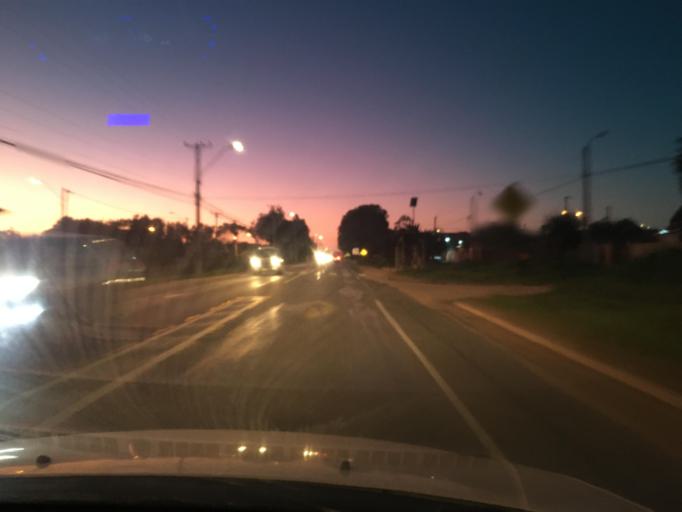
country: CL
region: Valparaiso
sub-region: San Antonio Province
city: El Tabo
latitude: -33.4291
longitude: -71.6894
